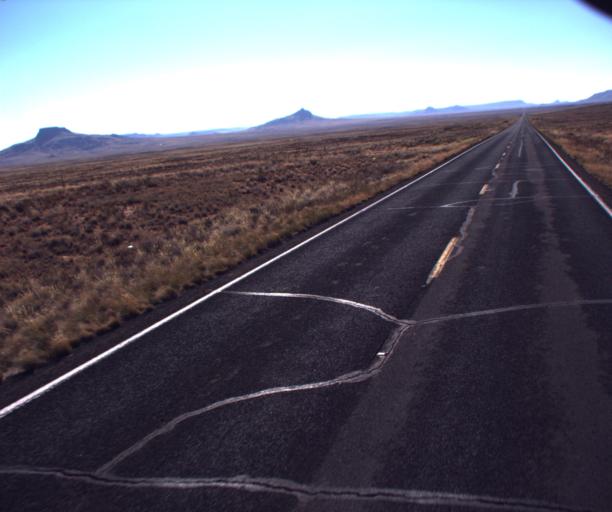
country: US
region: Arizona
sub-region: Navajo County
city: First Mesa
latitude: 35.6104
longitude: -110.4747
